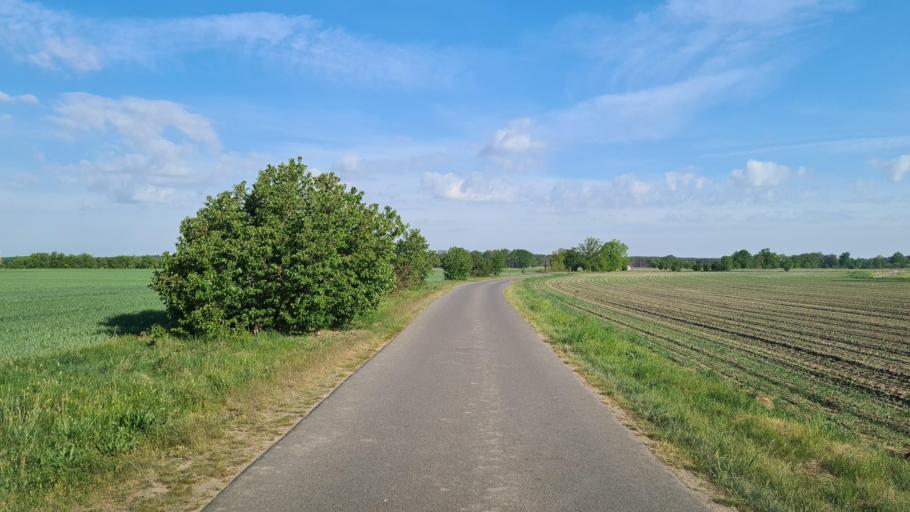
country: DE
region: Brandenburg
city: Falkenberg
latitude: 51.5877
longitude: 13.2066
